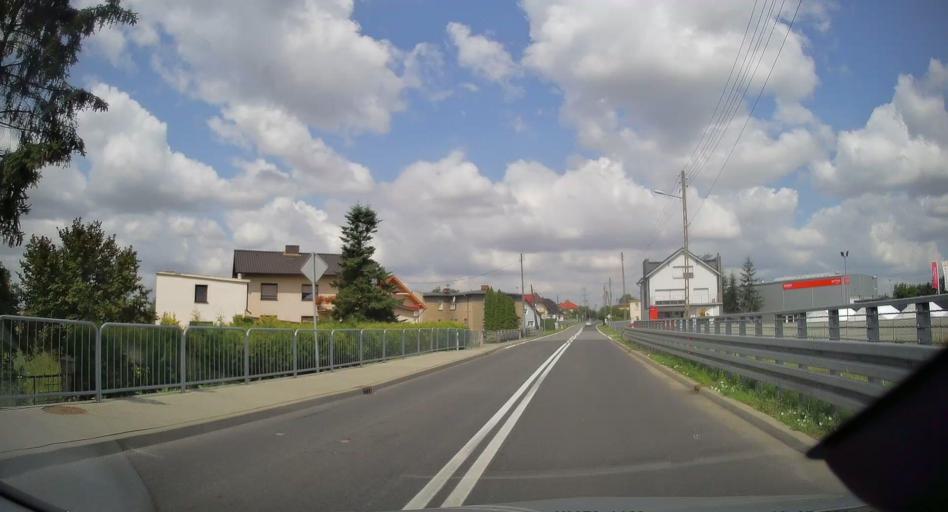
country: PL
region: Opole Voivodeship
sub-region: Powiat kedzierzynsko-kozielski
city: Wiekszyce
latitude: 50.3328
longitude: 18.0620
